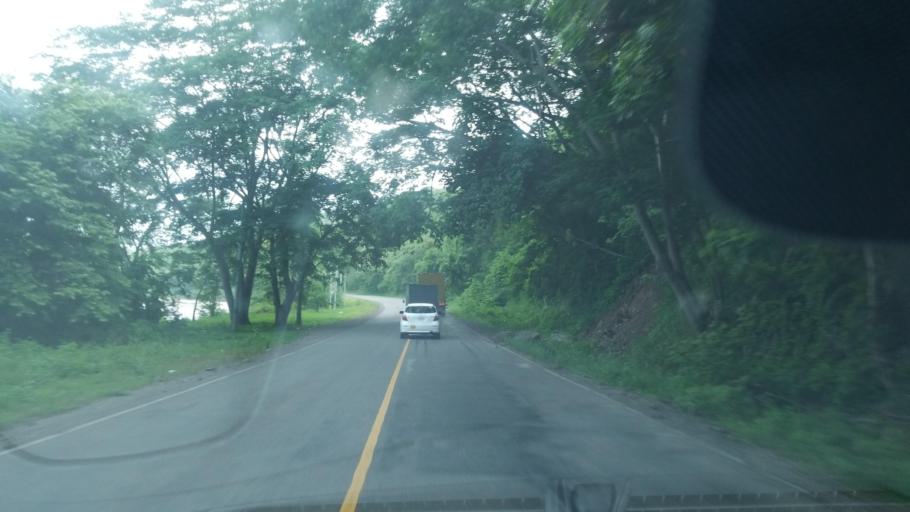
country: HN
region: Santa Barbara
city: Ilama
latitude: 15.0815
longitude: -88.2223
